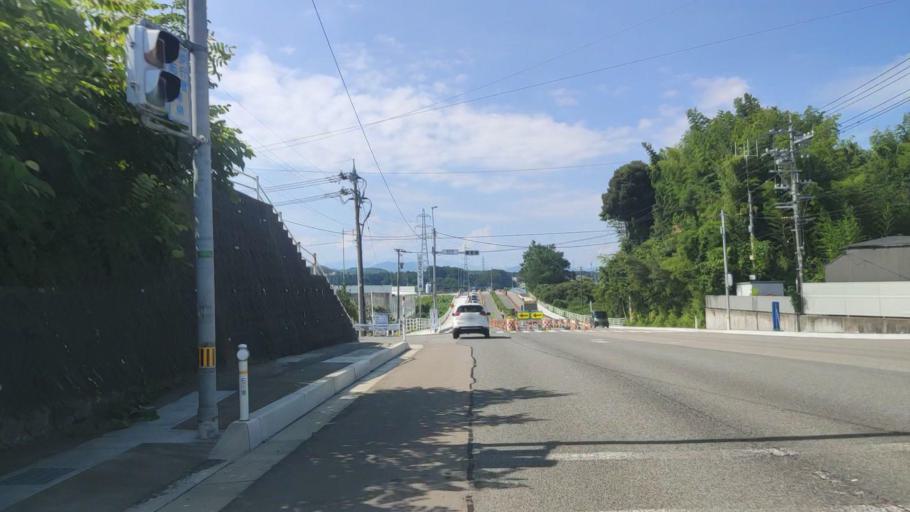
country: JP
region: Ishikawa
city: Komatsu
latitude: 36.4083
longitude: 136.5084
